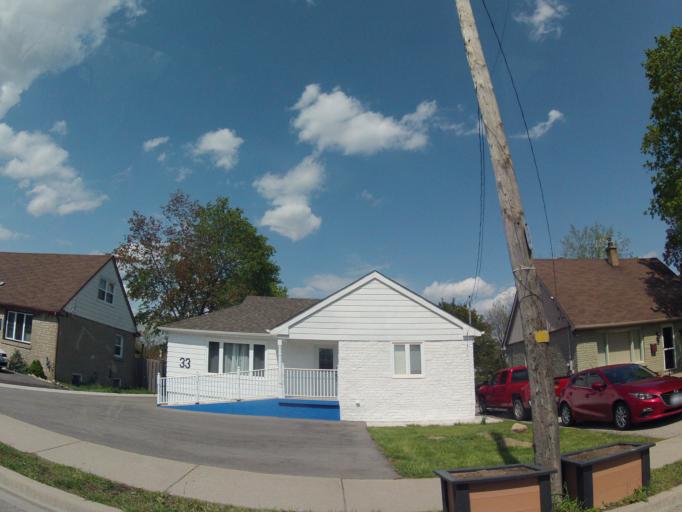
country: CA
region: Ontario
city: Mississauga
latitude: 43.5864
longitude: -79.7200
